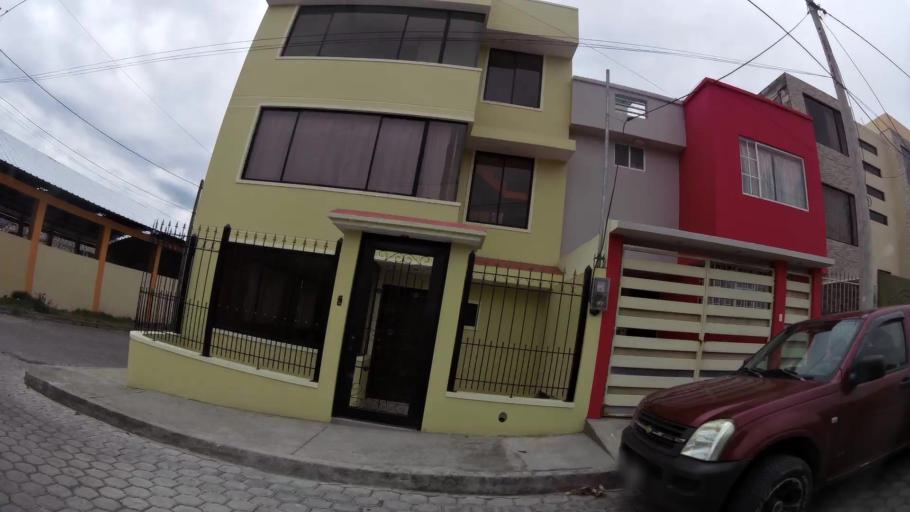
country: EC
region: Cotopaxi
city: Latacunga
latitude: -0.9556
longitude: -78.6034
